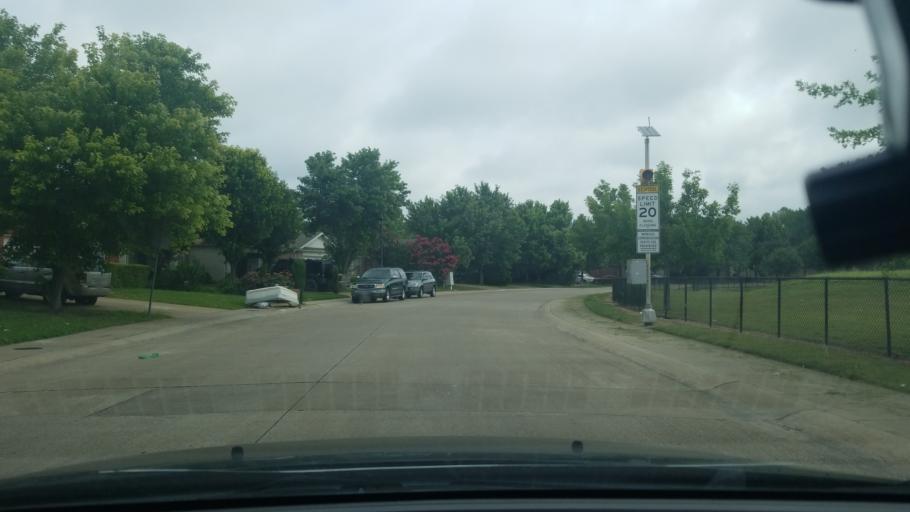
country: US
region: Texas
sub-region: Dallas County
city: Balch Springs
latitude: 32.7842
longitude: -96.6936
